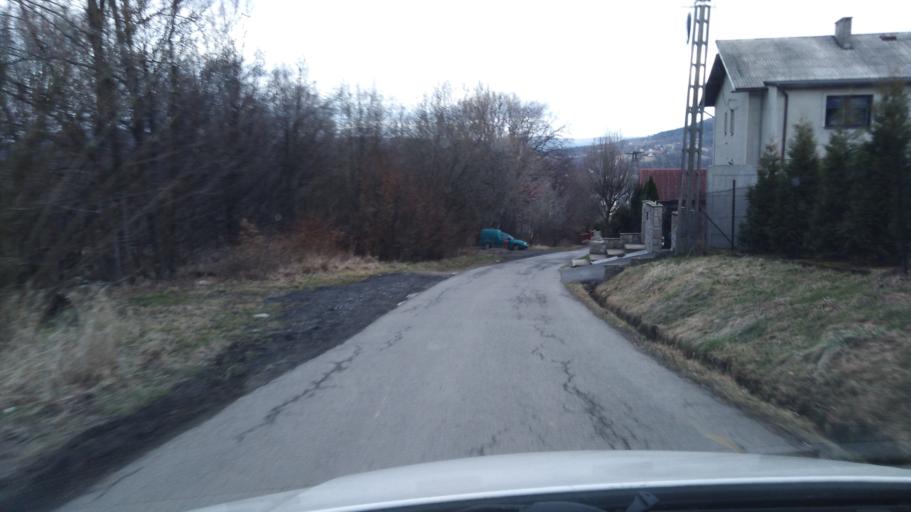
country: PL
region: Silesian Voivodeship
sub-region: Powiat zywiecki
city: Trzebinia
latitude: 49.6644
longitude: 19.2172
